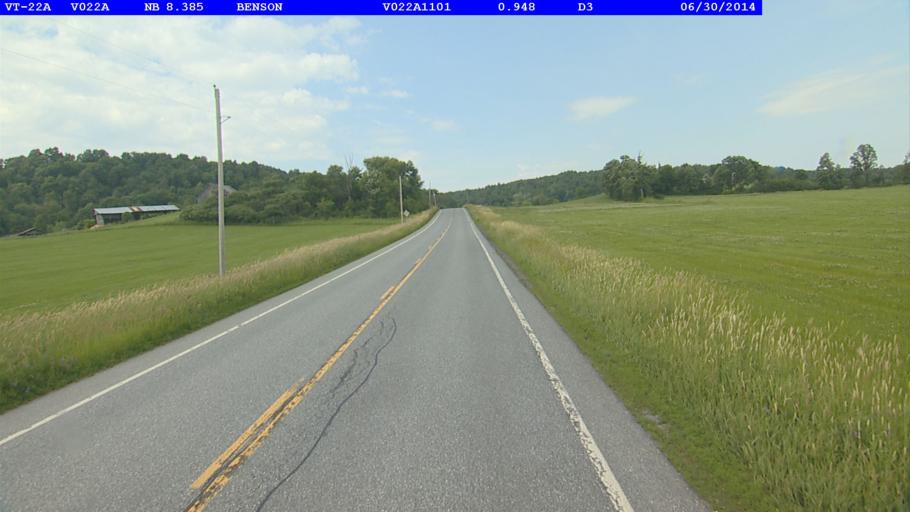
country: US
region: Vermont
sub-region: Rutland County
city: Fair Haven
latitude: 43.6827
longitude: -73.2894
